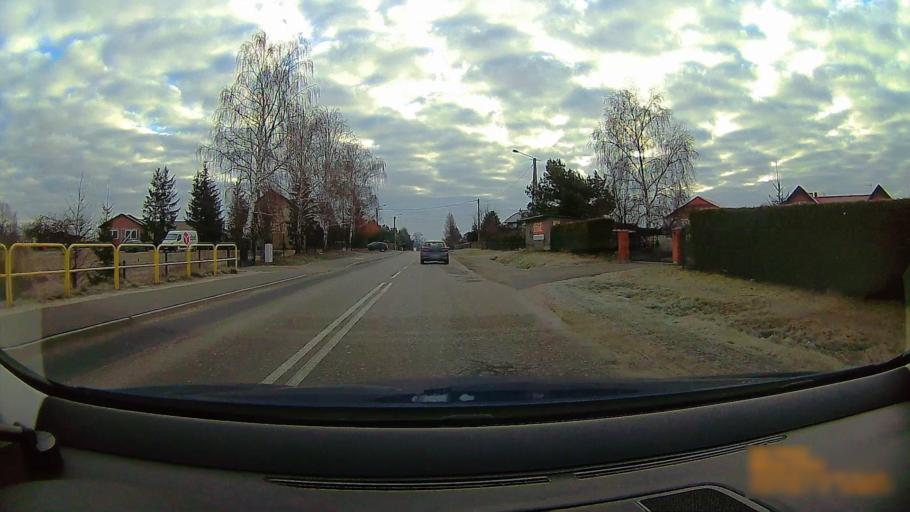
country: PL
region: Greater Poland Voivodeship
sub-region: Powiat koninski
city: Stare Miasto
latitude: 52.1996
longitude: 18.1478
